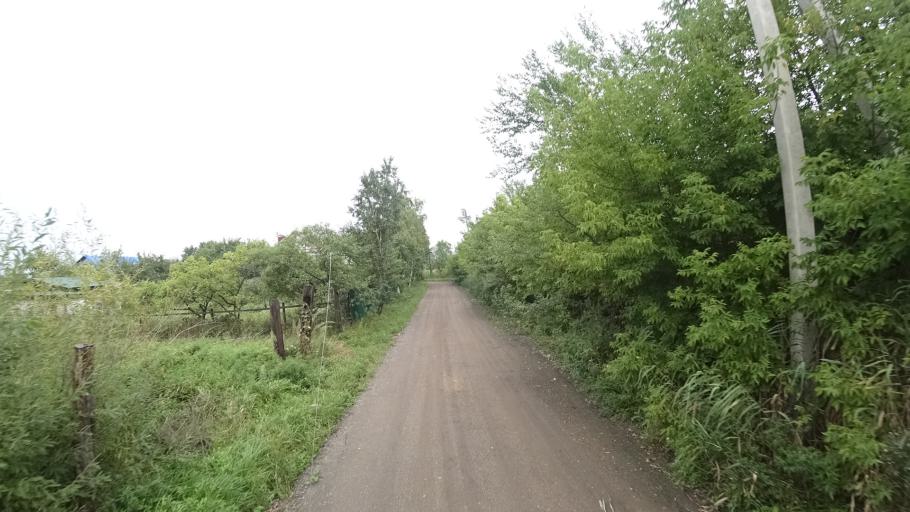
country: RU
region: Primorskiy
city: Chernigovka
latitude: 44.3323
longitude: 132.5697
